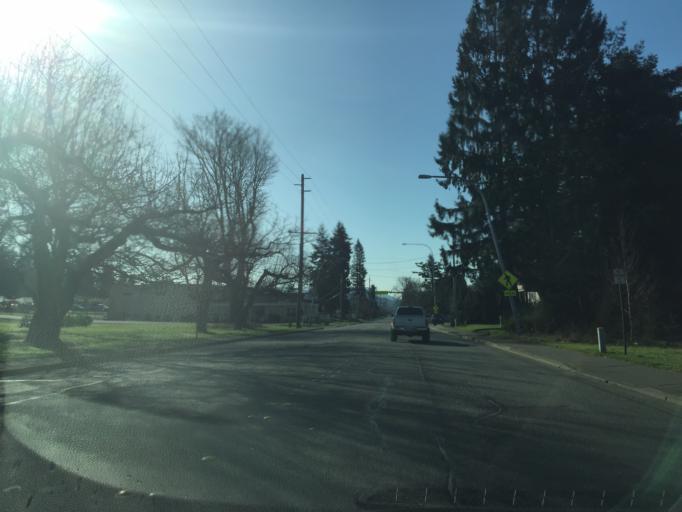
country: US
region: Washington
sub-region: Whatcom County
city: Bellingham
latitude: 48.7748
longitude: -122.4861
